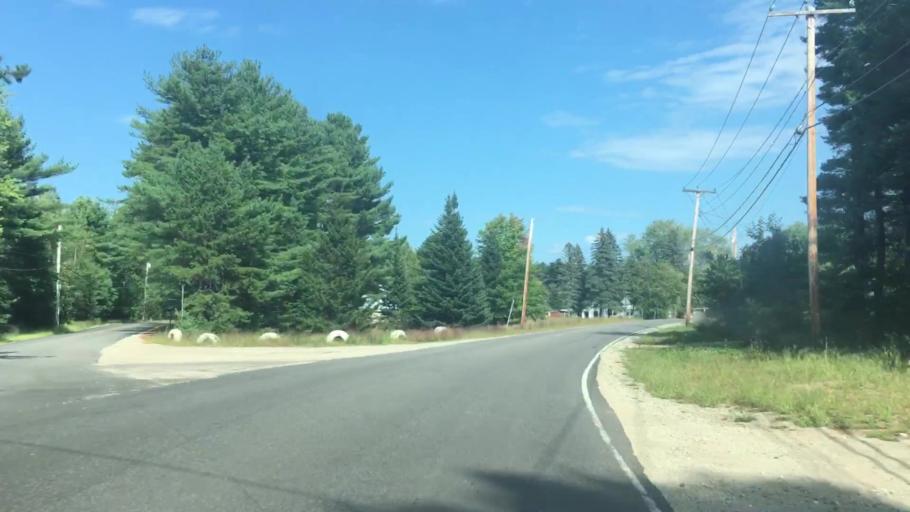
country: US
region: Maine
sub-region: Oxford County
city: Oxford
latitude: 44.1403
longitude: -70.4855
